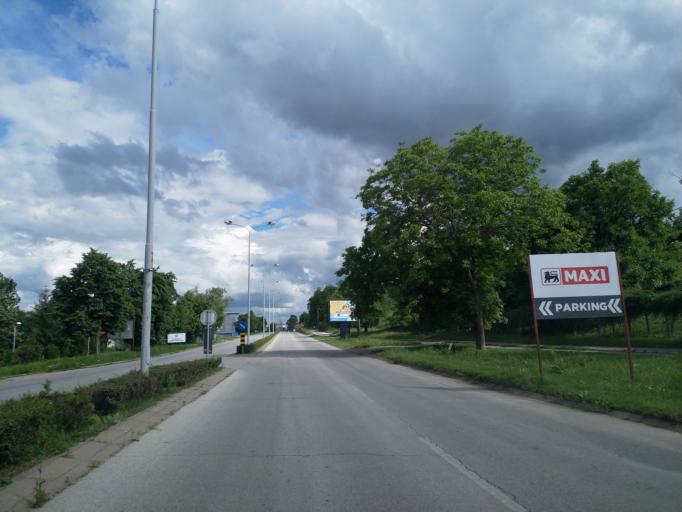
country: RS
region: Central Serbia
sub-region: Pomoravski Okrug
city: Jagodina
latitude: 43.9662
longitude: 21.2757
